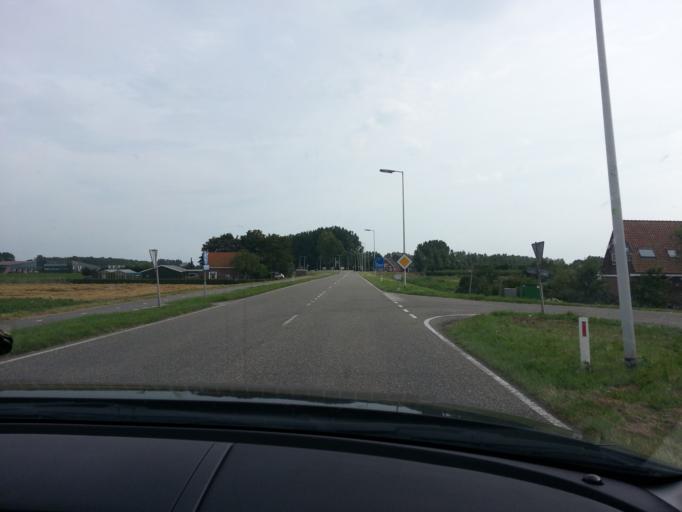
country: NL
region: South Holland
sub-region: Gemeente Spijkenisse
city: Spijkenisse
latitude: 51.8396
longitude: 4.2497
